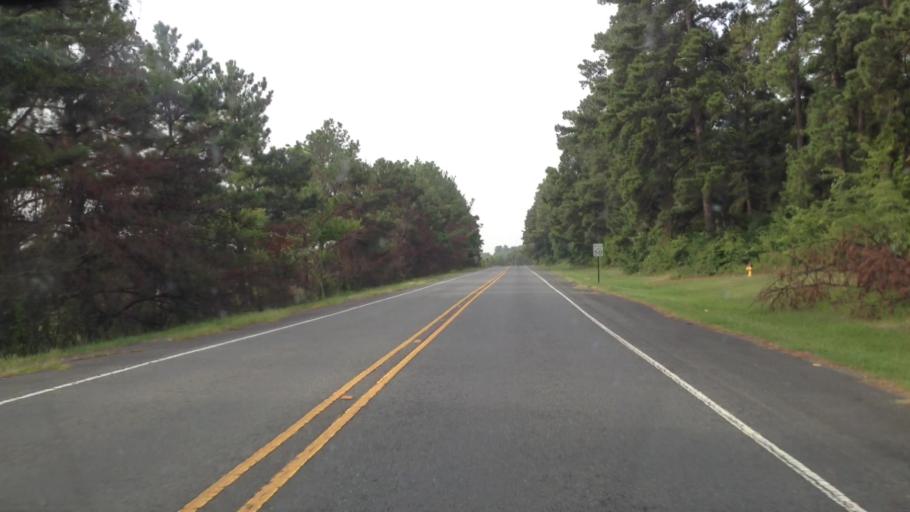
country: US
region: Louisiana
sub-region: Caddo Parish
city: Shreveport
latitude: 32.4521
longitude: -93.8440
